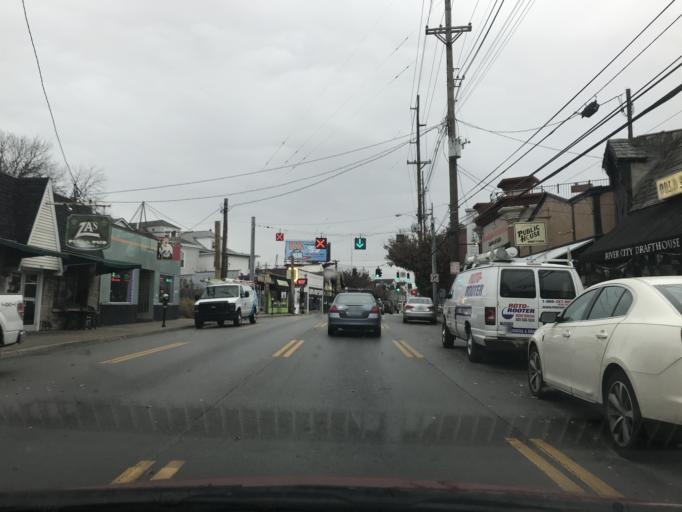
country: US
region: Kentucky
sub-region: Jefferson County
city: Audubon Park
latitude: 38.2309
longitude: -85.7052
